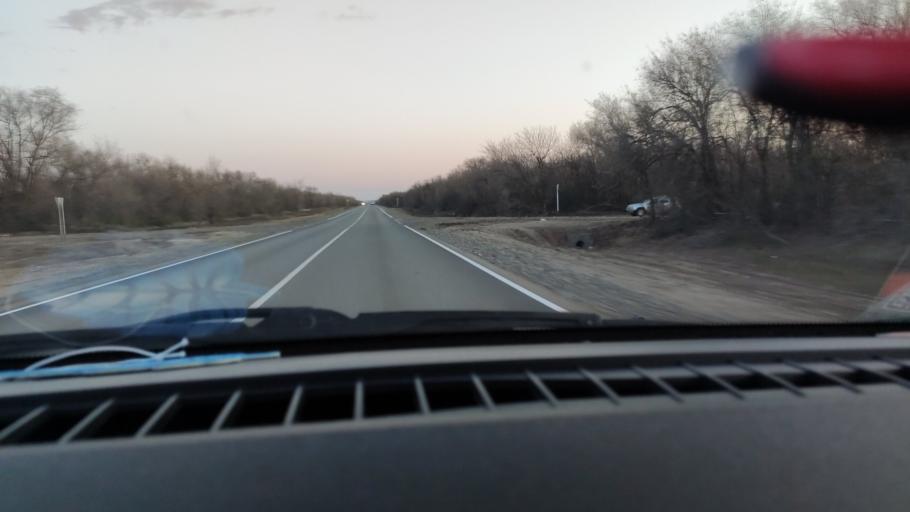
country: RU
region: Saratov
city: Privolzhskiy
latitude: 51.1455
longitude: 45.9616
